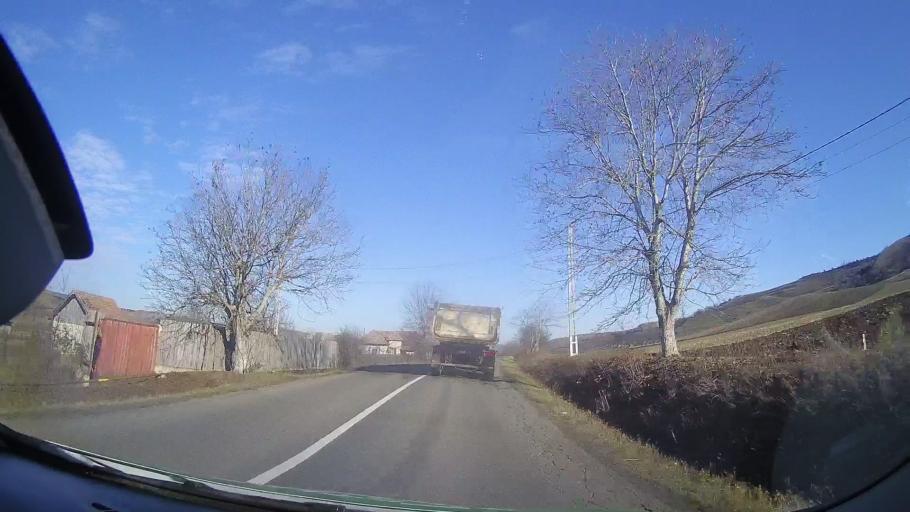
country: RO
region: Mures
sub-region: Comuna Iclanzel
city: Iclanzel
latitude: 46.5434
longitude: 24.3213
